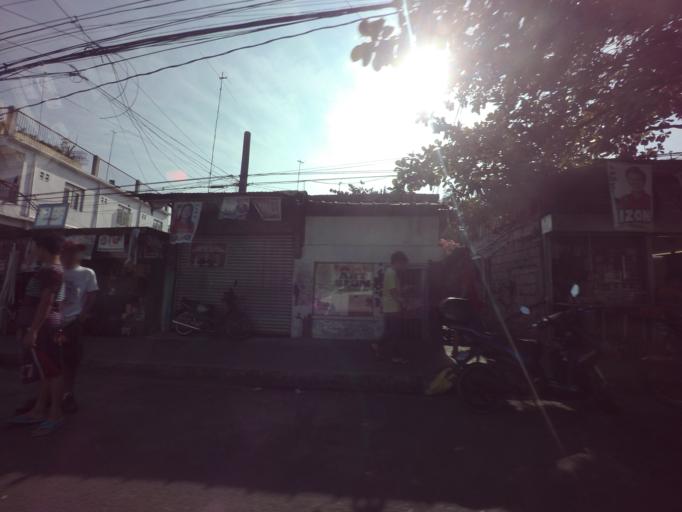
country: PH
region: Calabarzon
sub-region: Province of Rizal
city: Taguig
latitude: 14.5003
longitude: 121.0497
